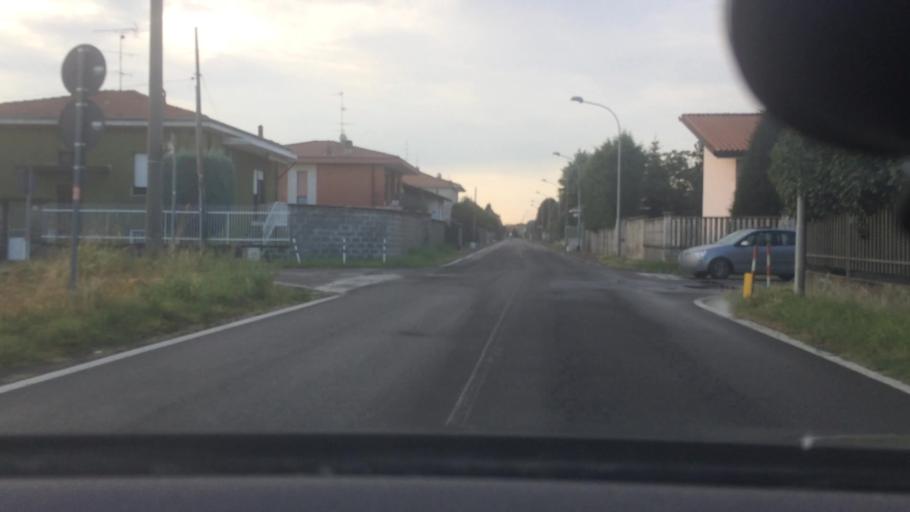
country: IT
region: Lombardy
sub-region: Citta metropolitana di Milano
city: Busto Garolfo
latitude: 45.5473
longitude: 8.8930
